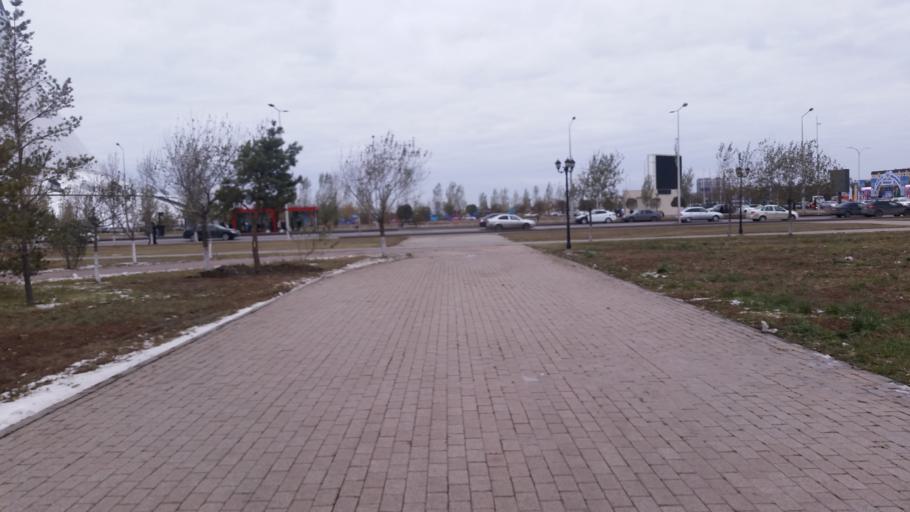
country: KZ
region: Astana Qalasy
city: Astana
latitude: 51.1335
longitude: 71.4083
